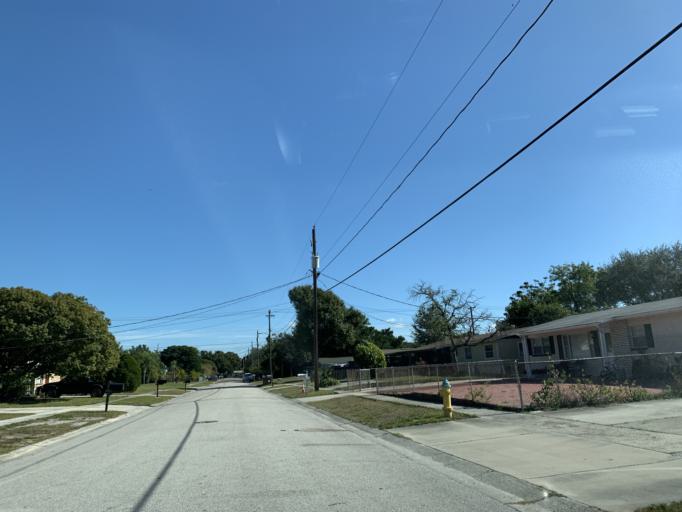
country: US
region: Florida
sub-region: Hillsborough County
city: Tampa
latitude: 27.8860
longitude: -82.5051
